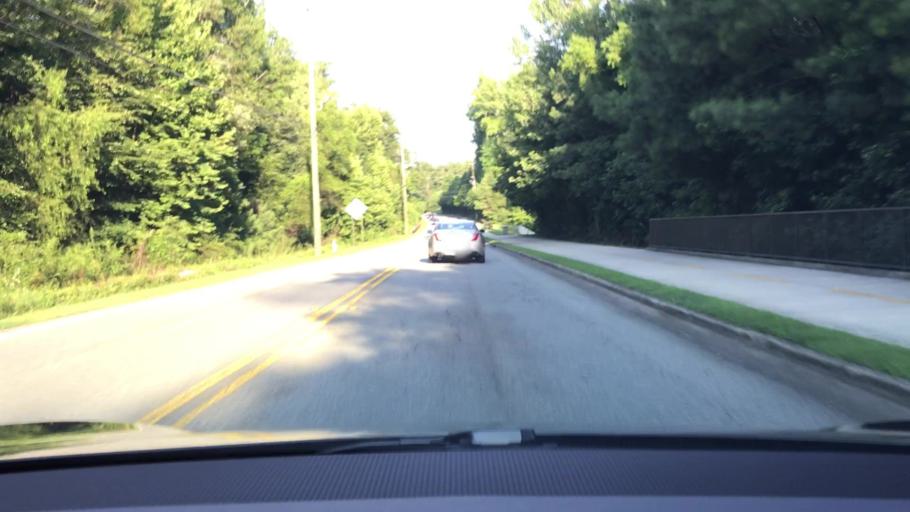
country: US
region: Georgia
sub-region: Fulton County
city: Alpharetta
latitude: 34.0778
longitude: -84.2491
